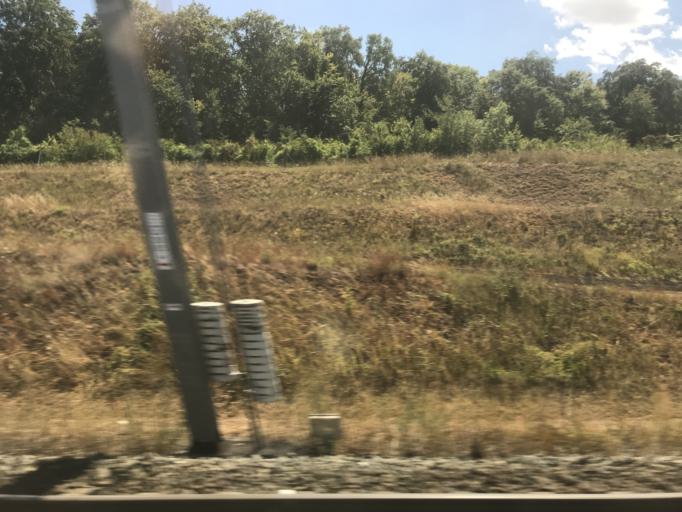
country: FR
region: Lorraine
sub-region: Departement de Meurthe-et-Moselle
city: Pagny-sur-Moselle
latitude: 48.9683
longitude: 5.9439
